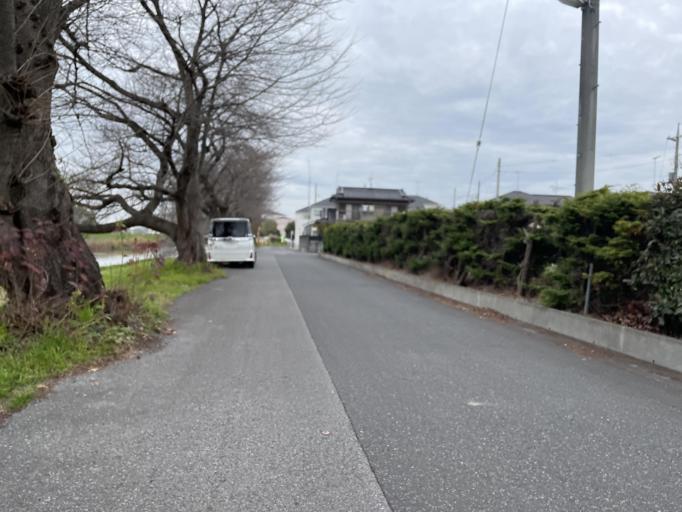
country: JP
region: Saitama
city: Shiraoka
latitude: 36.0259
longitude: 139.6496
